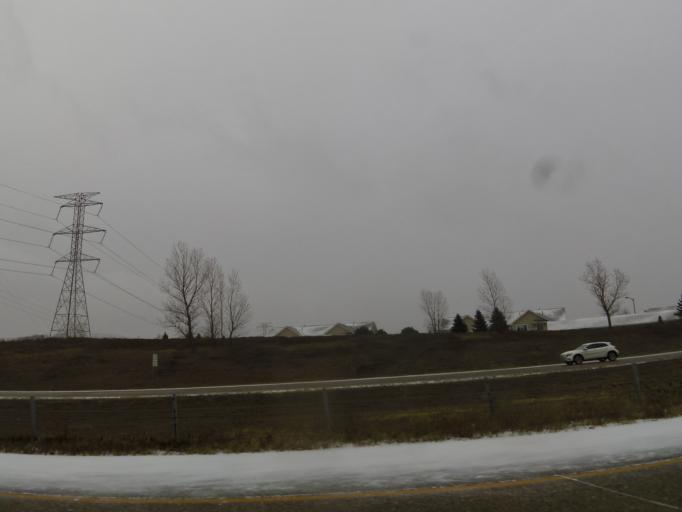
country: US
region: Minnesota
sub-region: Dakota County
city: Eagan
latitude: 44.7966
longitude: -93.2222
